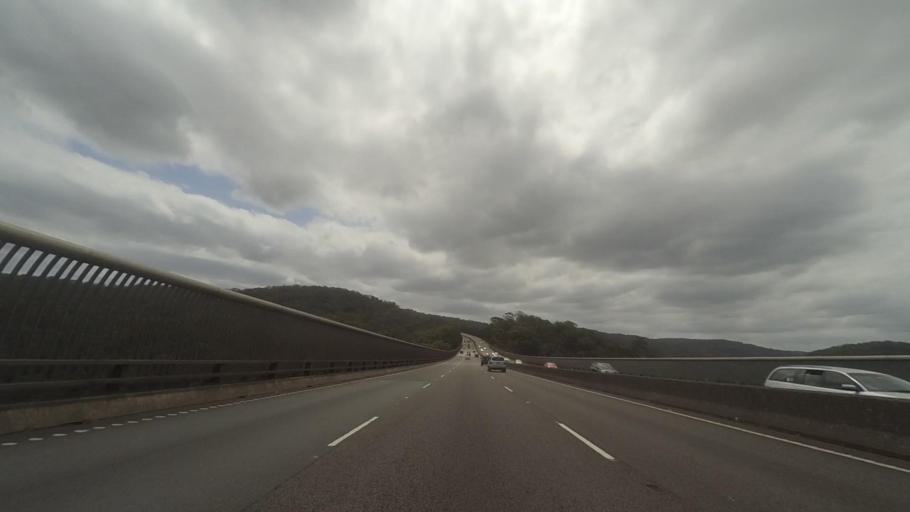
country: AU
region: New South Wales
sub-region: Gosford Shire
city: Point Clare
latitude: -33.4333
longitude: 151.2561
